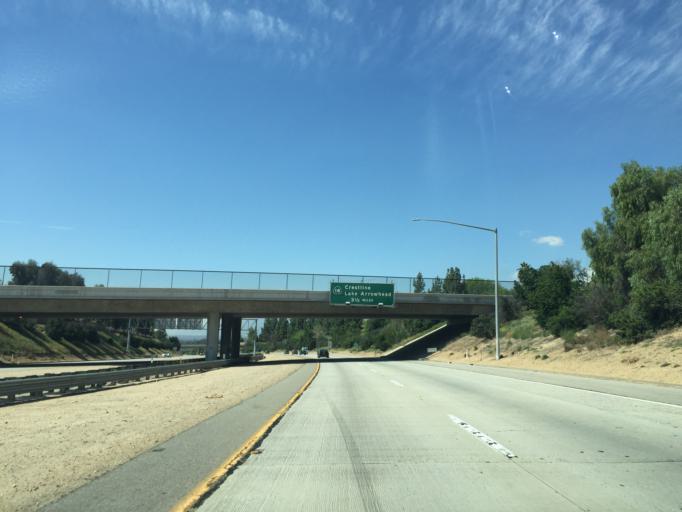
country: US
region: California
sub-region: San Bernardino County
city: Highland
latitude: 34.1314
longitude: -117.2079
